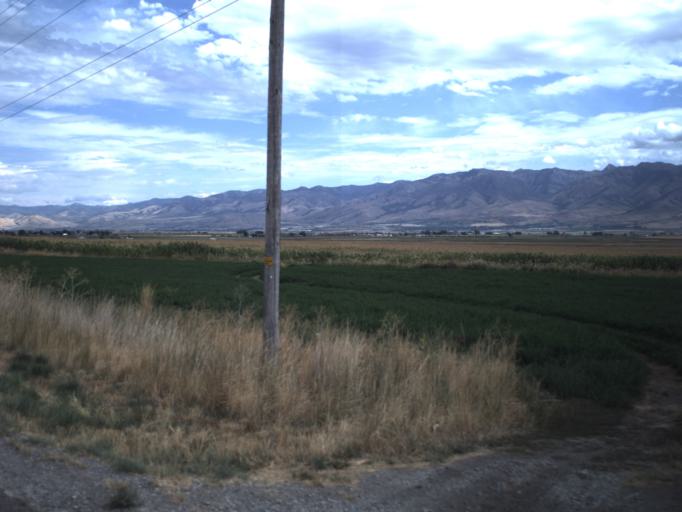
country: US
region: Utah
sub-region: Cache County
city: Benson
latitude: 41.8712
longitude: -111.9501
